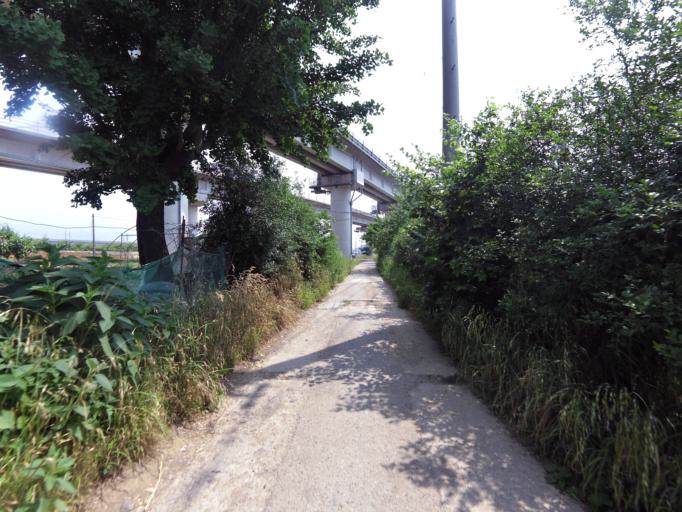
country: KR
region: Gyeongsangbuk-do
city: Gyeongsan-si
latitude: 35.8511
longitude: 128.7098
